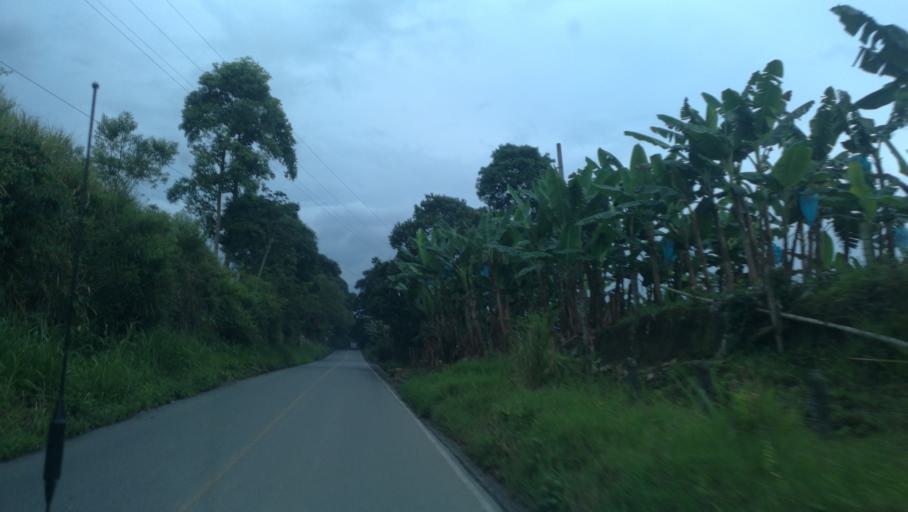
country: CO
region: Quindio
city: La Tebaida
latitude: 4.5093
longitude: -75.7788
